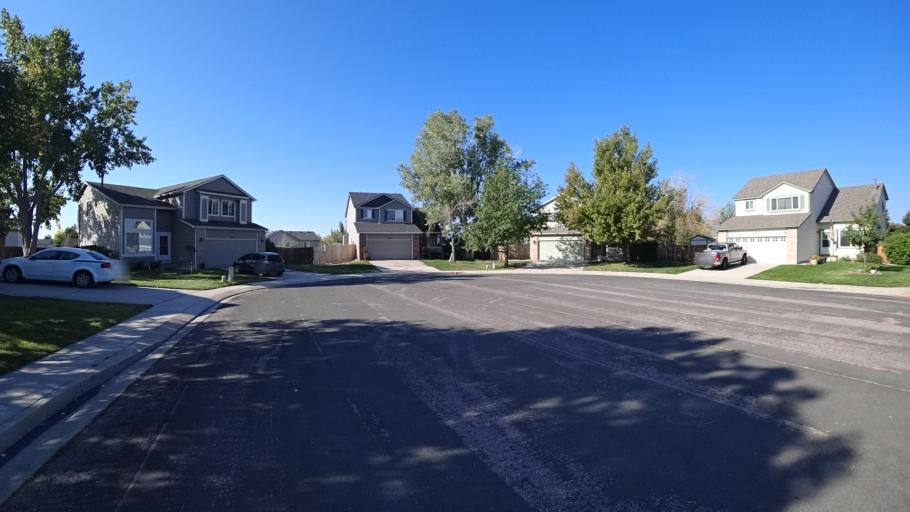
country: US
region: Colorado
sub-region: El Paso County
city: Cimarron Hills
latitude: 38.8815
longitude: -104.6955
